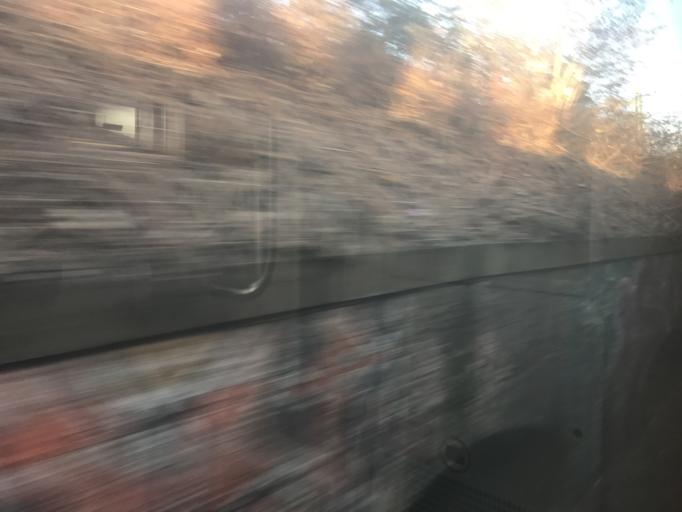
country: DE
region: North Rhine-Westphalia
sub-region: Regierungsbezirk Koln
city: Buchforst
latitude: 50.9481
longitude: 6.9949
